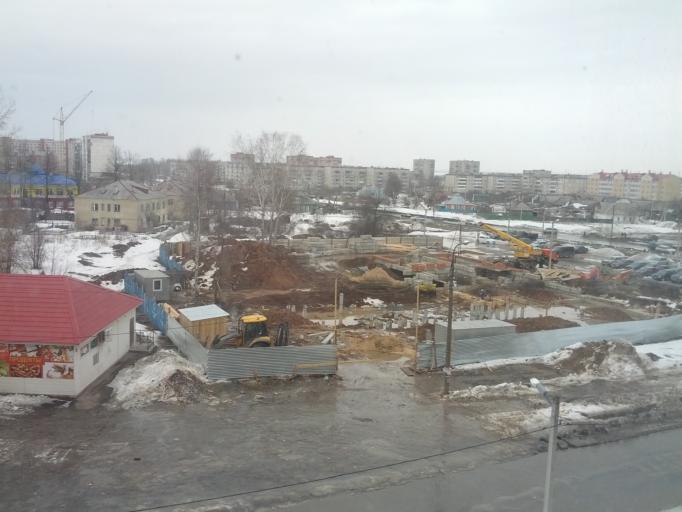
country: RU
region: Mariy-El
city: Yoshkar-Ola
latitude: 56.6453
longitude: 47.8554
